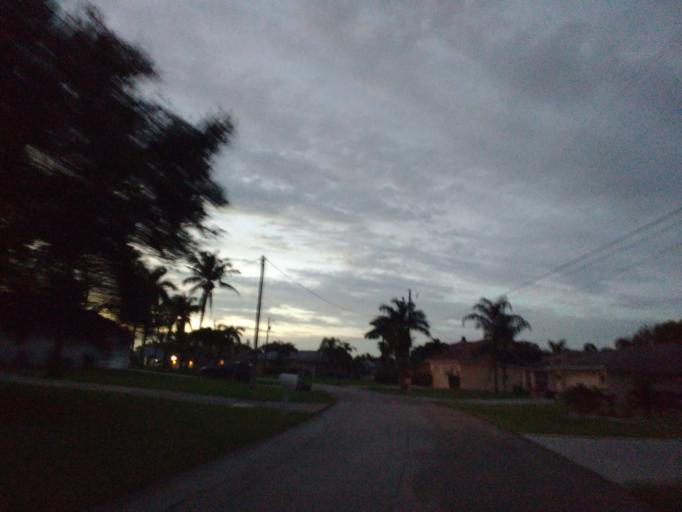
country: US
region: Florida
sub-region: Lee County
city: Lochmoor Waterway Estates
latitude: 26.6199
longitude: -81.9629
